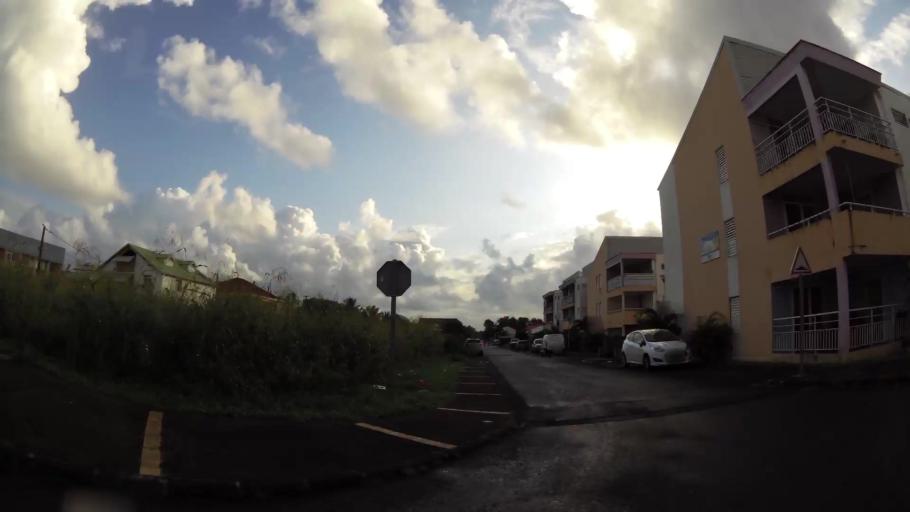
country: GP
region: Guadeloupe
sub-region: Guadeloupe
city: Petit-Bourg
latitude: 16.1304
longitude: -61.5756
